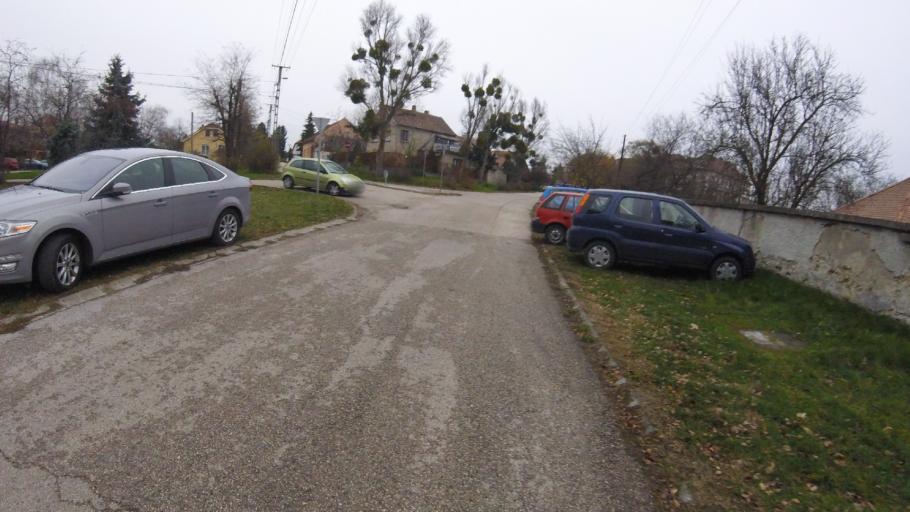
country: HU
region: Komarom-Esztergom
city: Tata
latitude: 47.6404
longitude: 18.3195
